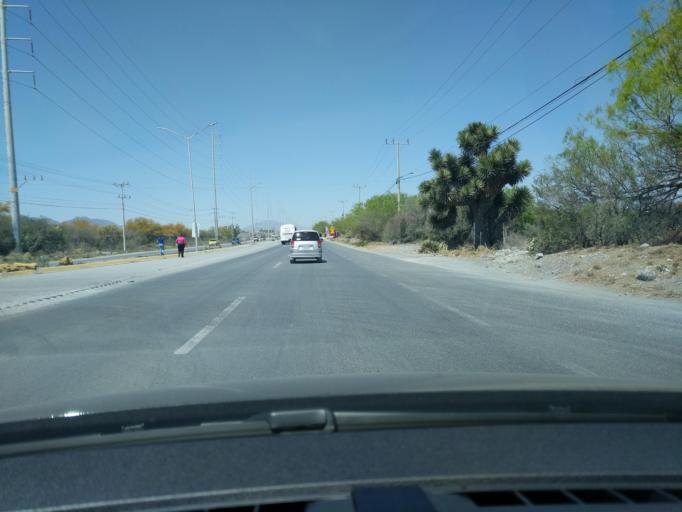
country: MX
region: Nuevo Leon
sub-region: Salinas Victoria
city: Emiliano Zapata
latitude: 25.9056
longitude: -100.2647
